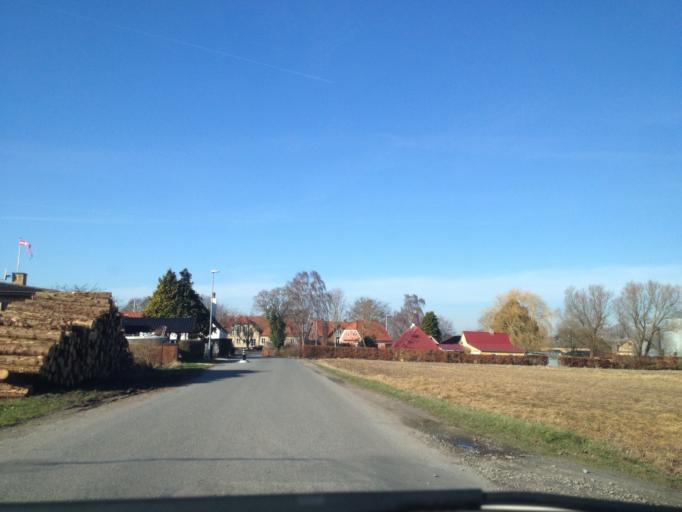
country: DK
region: South Denmark
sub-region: Nyborg Kommune
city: Ullerslev
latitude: 55.3852
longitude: 10.7087
